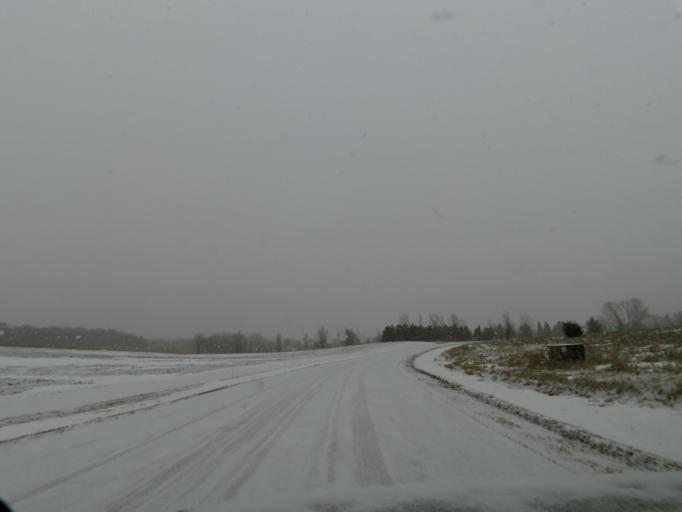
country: US
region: Minnesota
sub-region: Washington County
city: Lake Elmo
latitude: 44.9861
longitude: -92.8993
